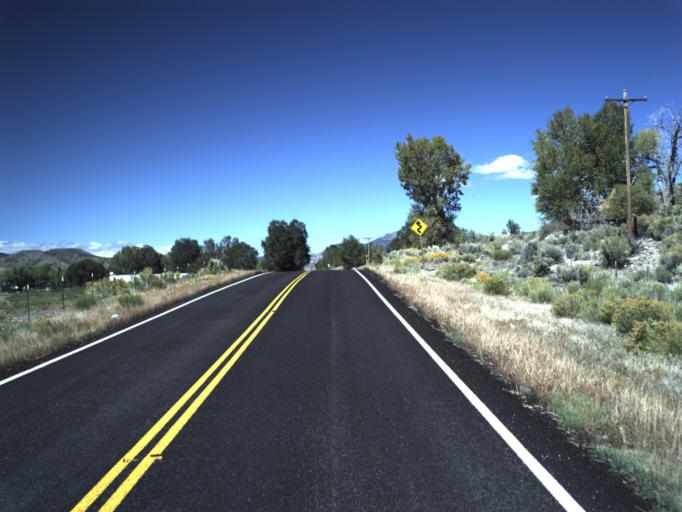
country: US
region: Utah
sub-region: Piute County
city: Junction
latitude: 38.1097
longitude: -111.9883
